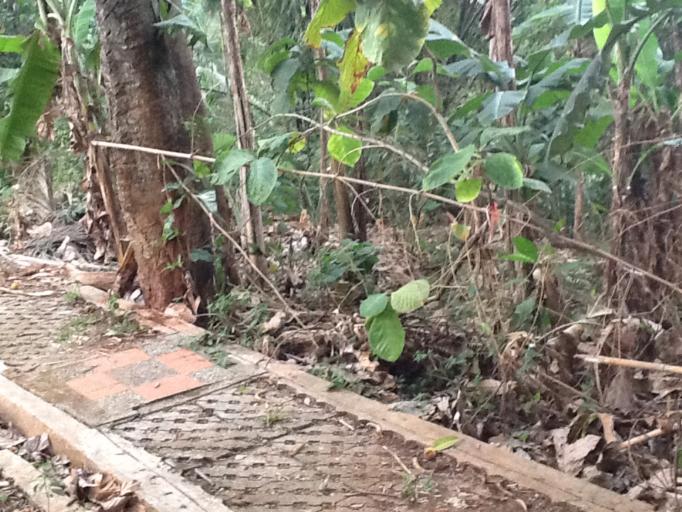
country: ID
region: West Java
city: Pamulang
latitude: -6.3152
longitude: 106.7783
